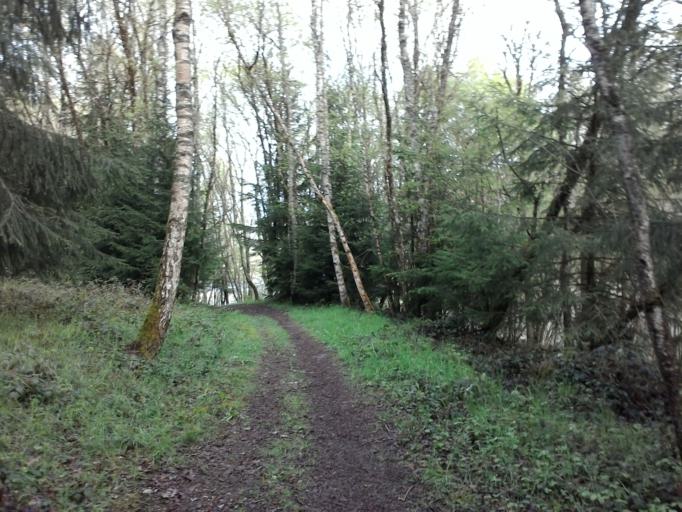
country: FR
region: Bourgogne
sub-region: Departement de la Cote-d'Or
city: Saulieu
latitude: 47.2511
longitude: 4.1975
